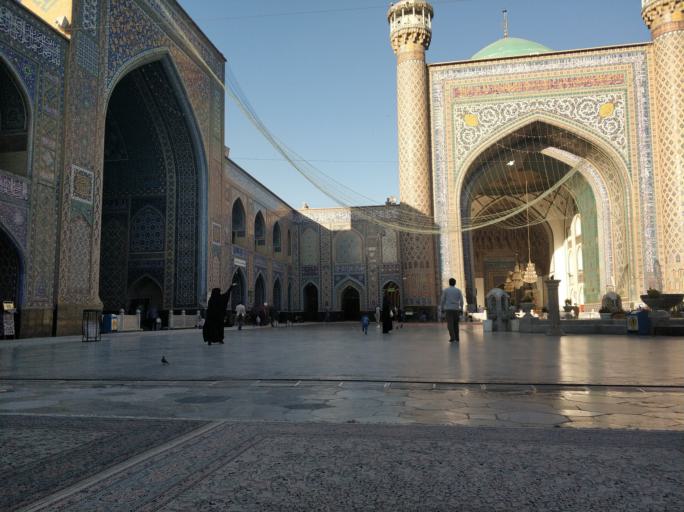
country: IR
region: Razavi Khorasan
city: Mashhad
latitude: 36.2877
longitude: 59.6151
